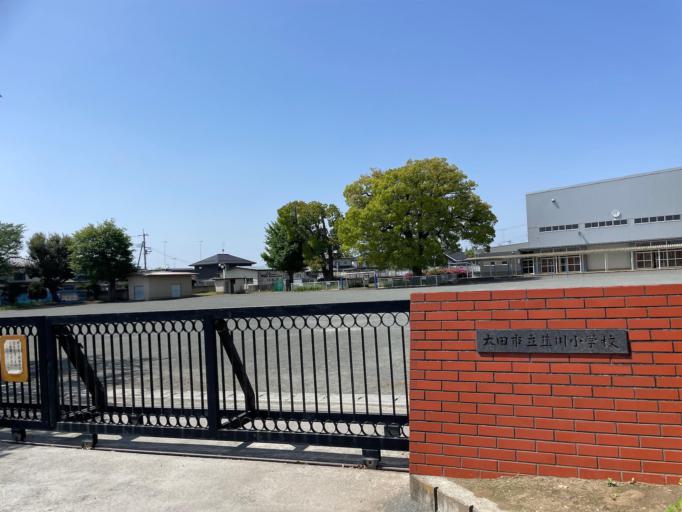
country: JP
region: Gunma
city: Ota
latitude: 36.3041
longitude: 139.4040
